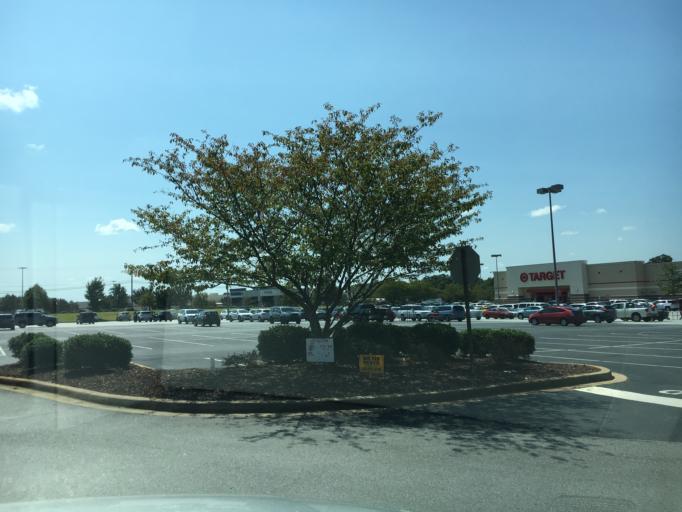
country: US
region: South Carolina
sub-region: Greenville County
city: Mauldin
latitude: 34.8311
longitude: -82.3073
